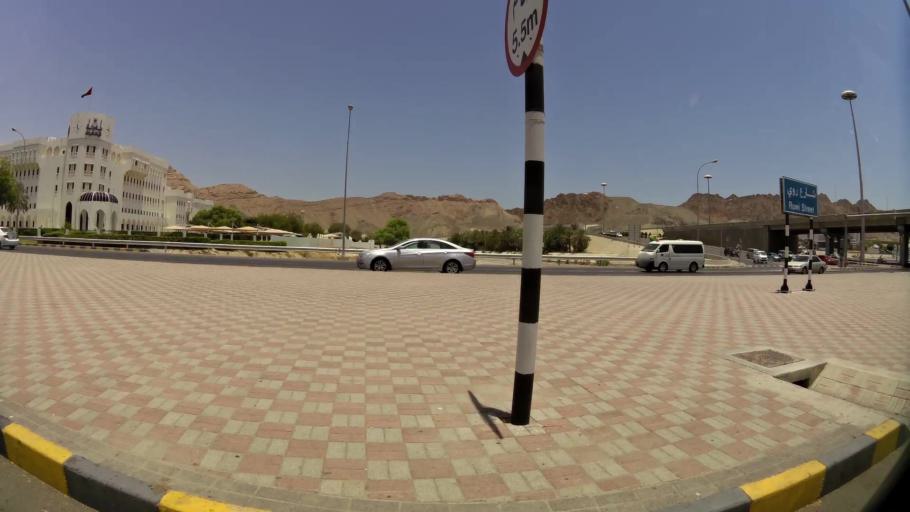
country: OM
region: Muhafazat Masqat
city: Muscat
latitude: 23.6150
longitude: 58.5447
